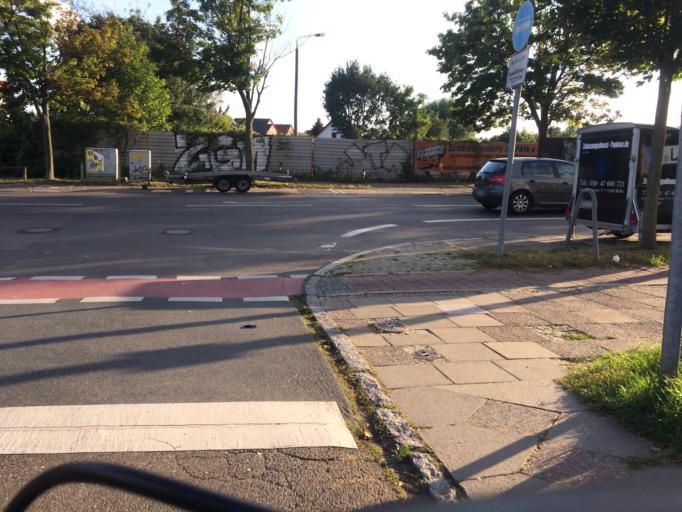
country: DE
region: Berlin
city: Heinersdorf
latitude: 52.5649
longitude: 13.4484
